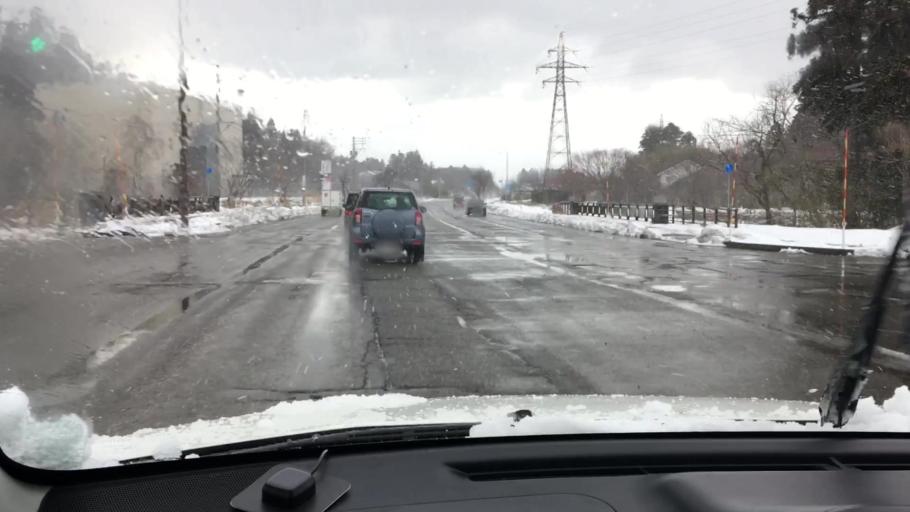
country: JP
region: Niigata
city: Joetsu
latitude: 37.0981
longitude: 138.2309
